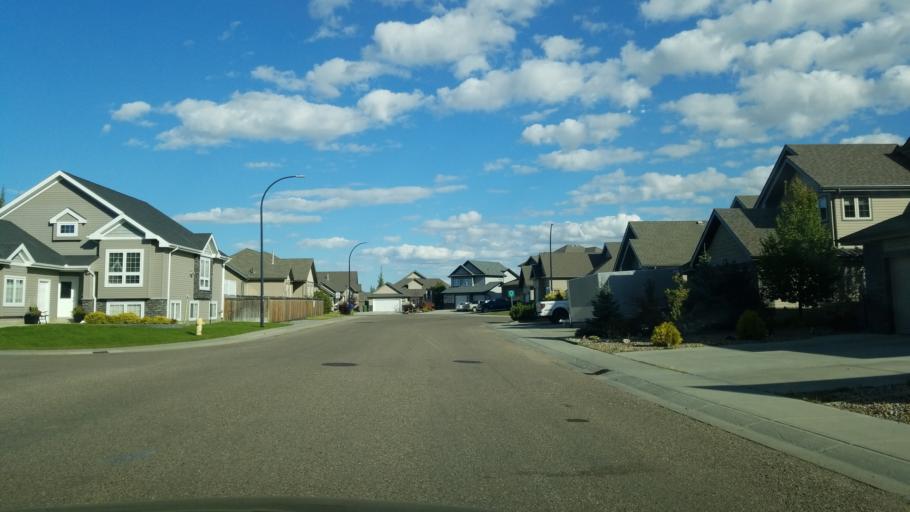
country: CA
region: Saskatchewan
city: Lloydminster
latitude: 53.2523
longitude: -110.0173
